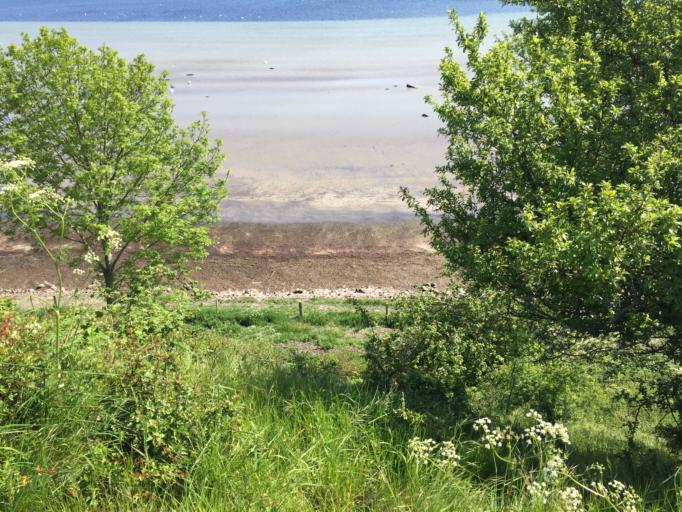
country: DK
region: Zealand
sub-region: Lolland Kommune
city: Maribo
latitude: 54.8964
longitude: 11.3615
